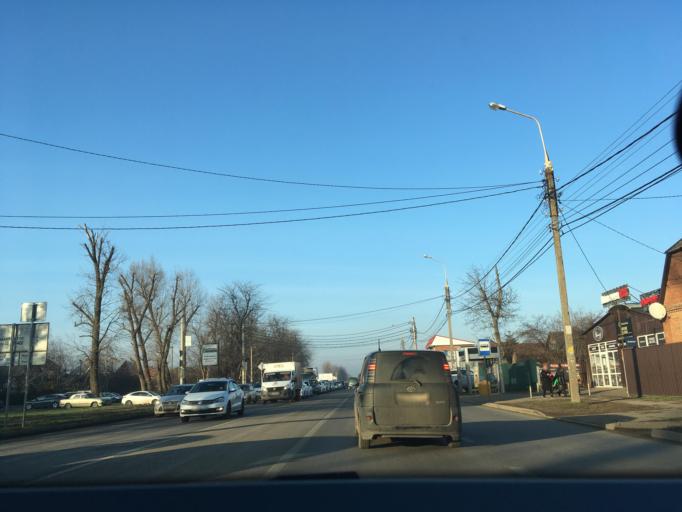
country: RU
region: Krasnodarskiy
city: Krasnodar
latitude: 45.0953
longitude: 39.0137
